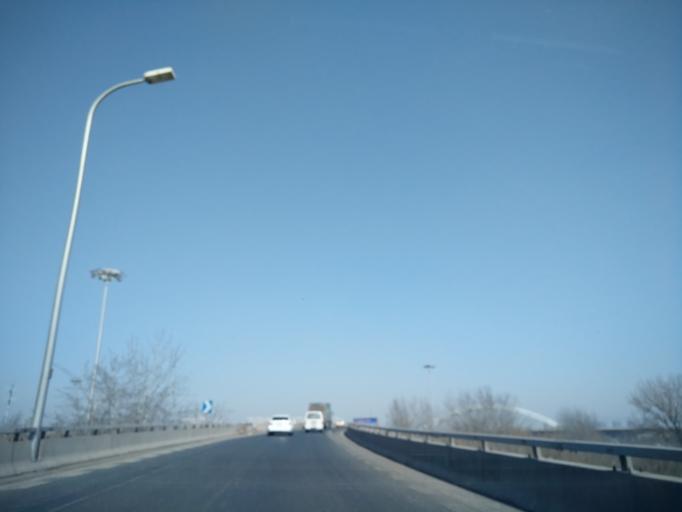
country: CN
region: Beijing
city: Jiugong
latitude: 39.8402
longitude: 116.4747
